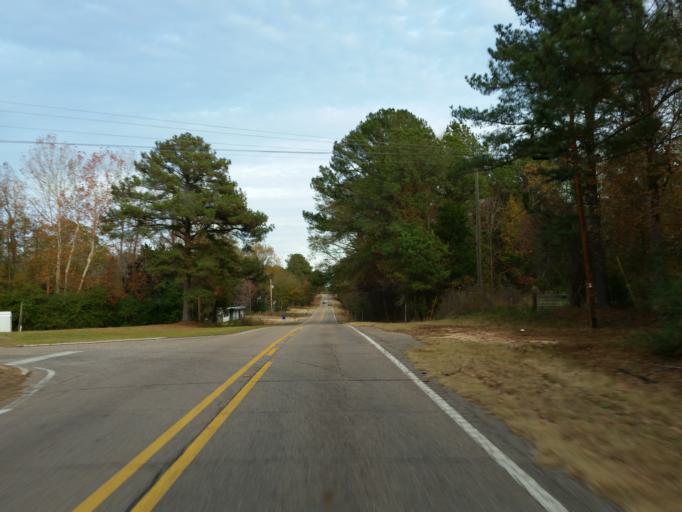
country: US
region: Mississippi
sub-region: Lauderdale County
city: Marion
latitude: 32.4224
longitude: -88.4808
